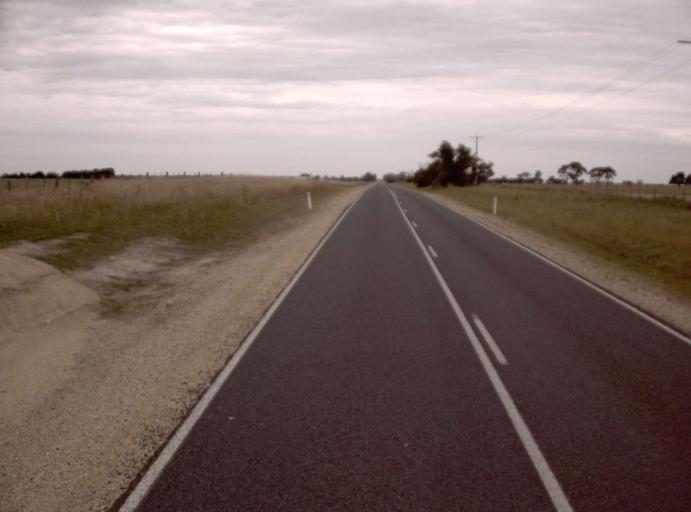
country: AU
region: Victoria
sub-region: Wellington
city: Sale
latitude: -38.1727
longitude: 147.1778
